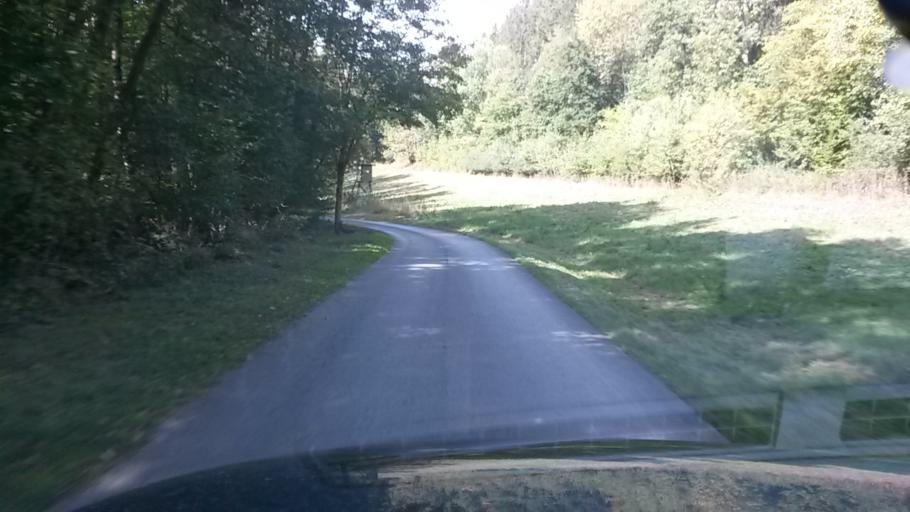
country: DE
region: North Rhine-Westphalia
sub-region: Regierungsbezirk Arnsberg
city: Herscheid
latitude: 51.1903
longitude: 7.7173
